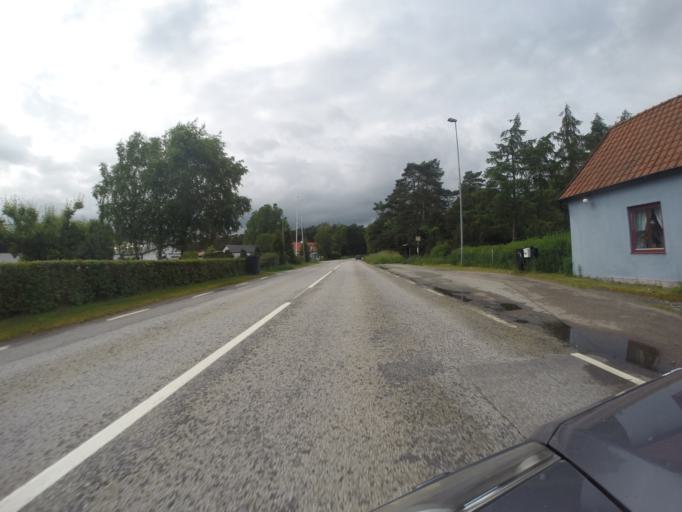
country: SE
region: Skane
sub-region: Kavlinge Kommun
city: Hofterup
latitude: 55.8308
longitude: 12.9637
